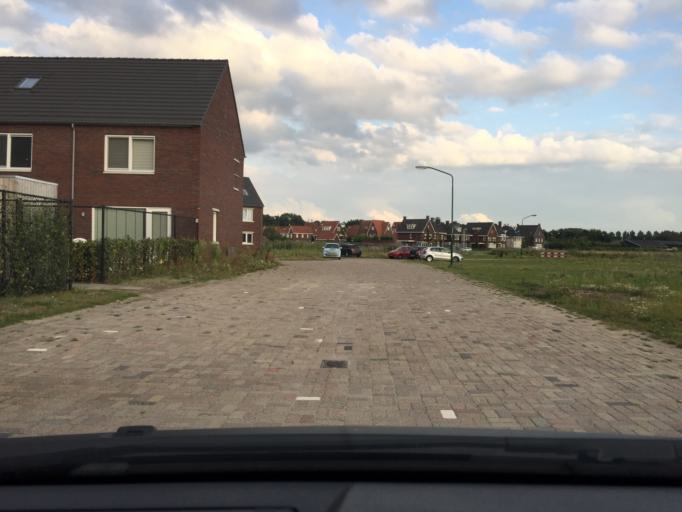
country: NL
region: North Brabant
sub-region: Gemeente Laarbeek
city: Aarle-Rixtel
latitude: 51.5245
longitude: 5.6343
